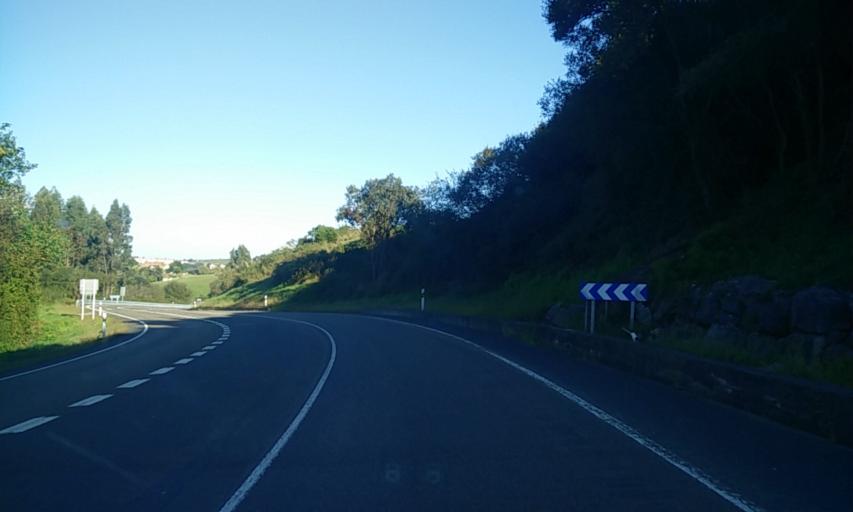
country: ES
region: Cantabria
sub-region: Provincia de Cantabria
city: San Vicente de la Barquera
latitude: 43.3817
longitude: -4.3811
